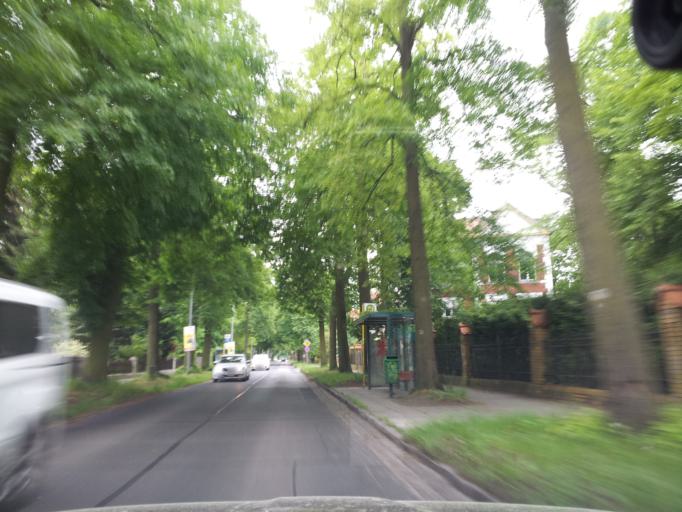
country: DE
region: Brandenburg
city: Dallgow-Doeberitz
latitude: 52.5590
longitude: 13.0500
